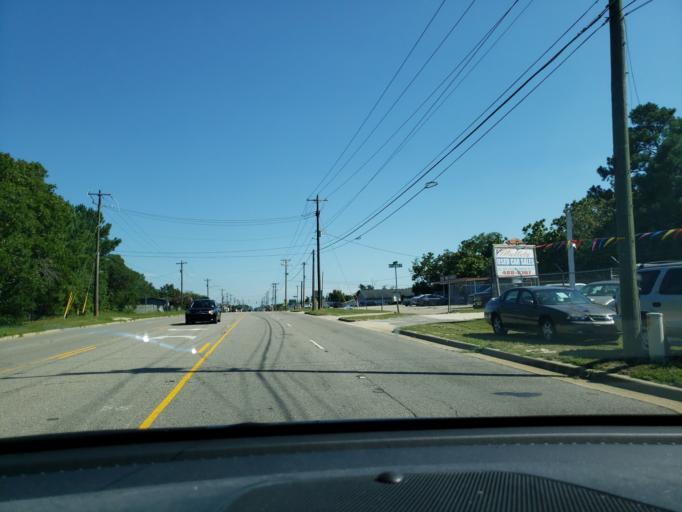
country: US
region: North Carolina
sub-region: Cumberland County
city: Spring Lake
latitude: 35.1167
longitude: -78.9321
